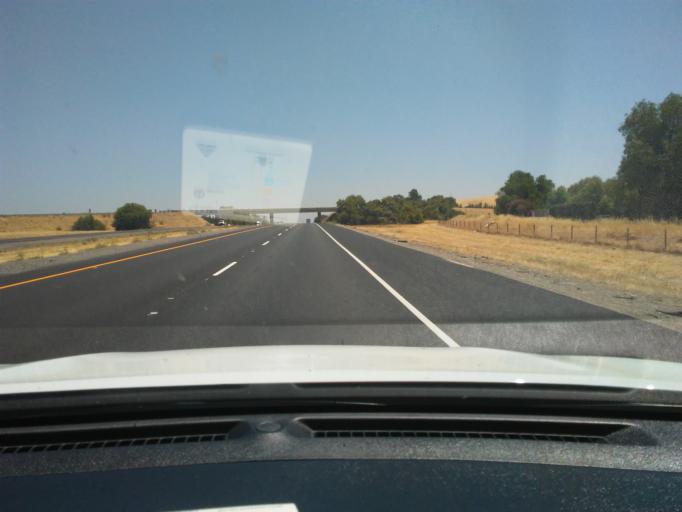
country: US
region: California
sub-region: San Joaquin County
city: Tracy
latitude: 37.6375
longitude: -121.4005
